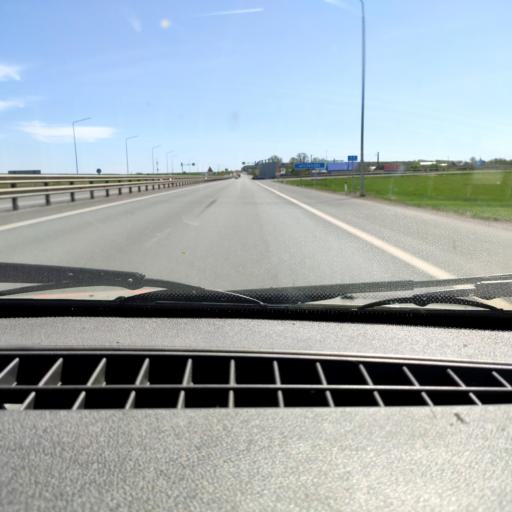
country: RU
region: Bashkortostan
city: Tolbazy
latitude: 54.1610
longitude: 55.9023
